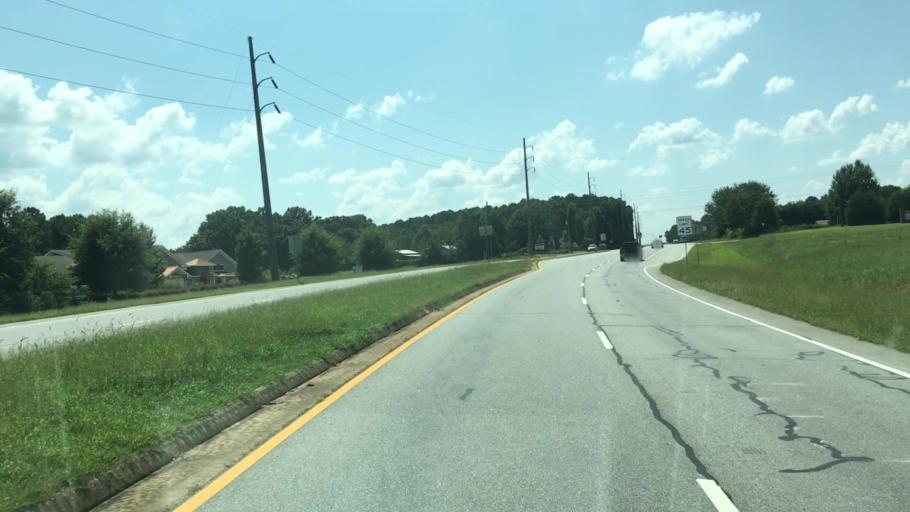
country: US
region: Georgia
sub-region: Morgan County
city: Madison
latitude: 33.5759
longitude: -83.4515
